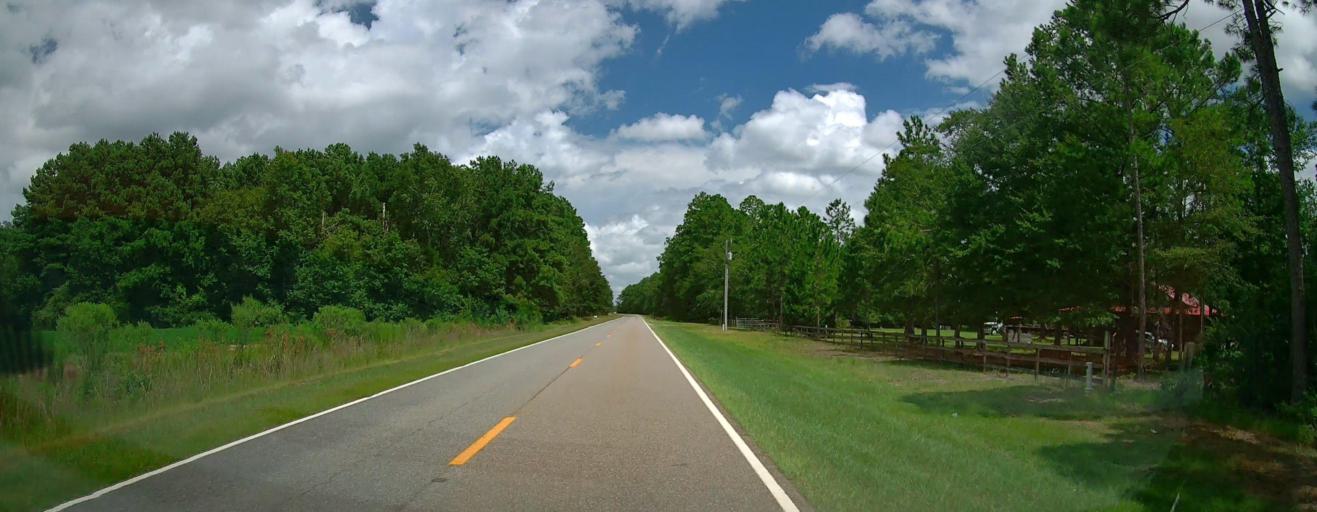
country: US
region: Georgia
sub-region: Irwin County
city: Ocilla
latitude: 31.6455
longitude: -83.3201
